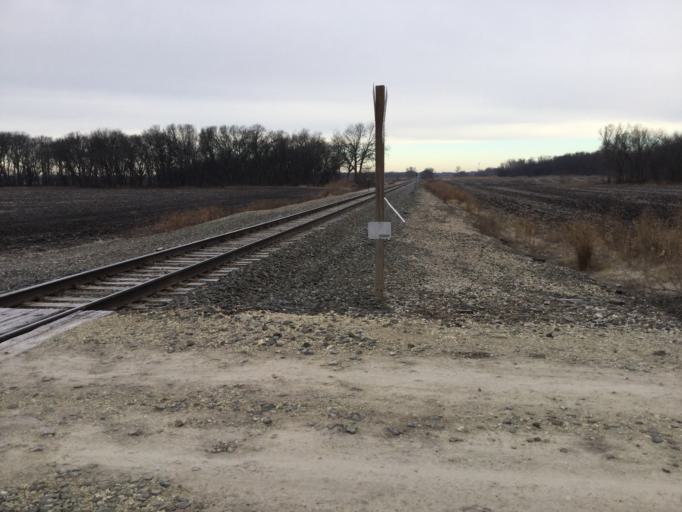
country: US
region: Kansas
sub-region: Butler County
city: Douglass
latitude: 37.4903
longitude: -97.0097
